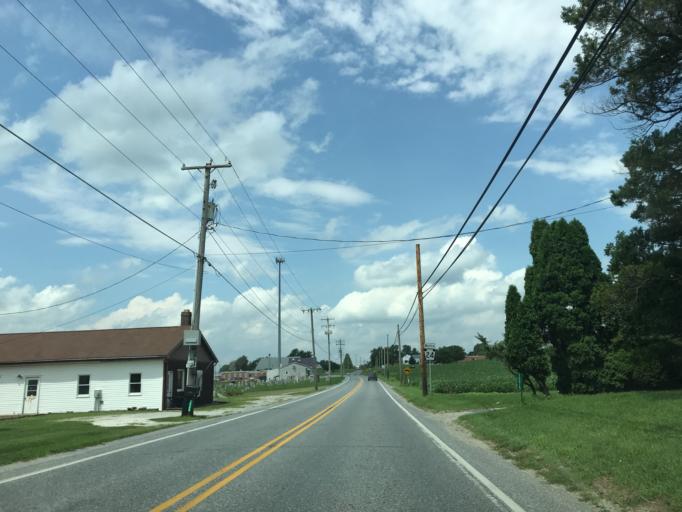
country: US
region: Pennsylvania
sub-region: York County
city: Red Lion
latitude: 39.8358
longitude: -76.6184
